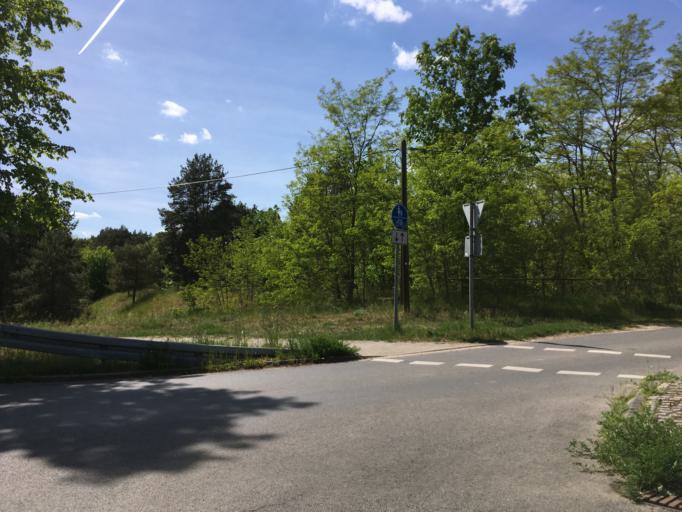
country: DE
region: Brandenburg
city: Oderberg
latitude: 52.8408
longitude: 14.1117
